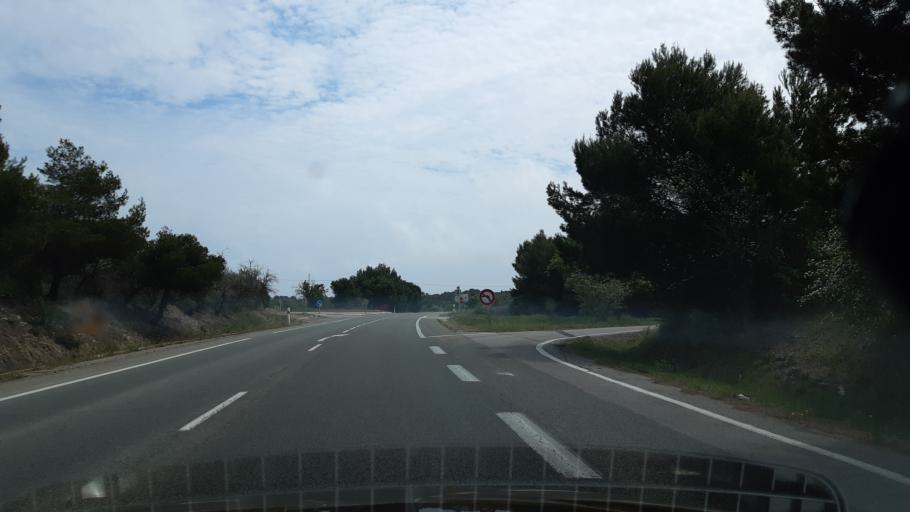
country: FR
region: Languedoc-Roussillon
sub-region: Departement de l'Aude
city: Gruissan
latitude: 43.1269
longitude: 3.0610
